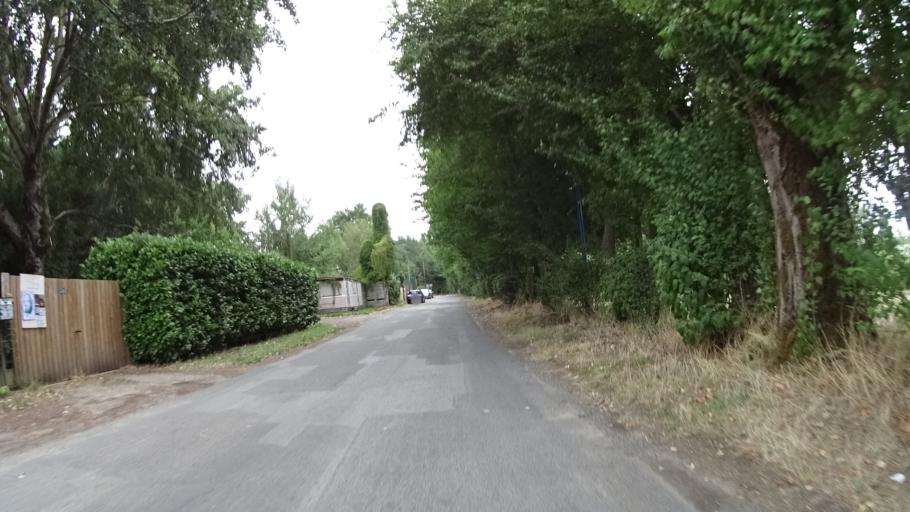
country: FR
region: Pays de la Loire
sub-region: Departement de la Loire-Atlantique
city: Sainte-Luce-sur-Loire
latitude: 47.2429
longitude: -1.4643
